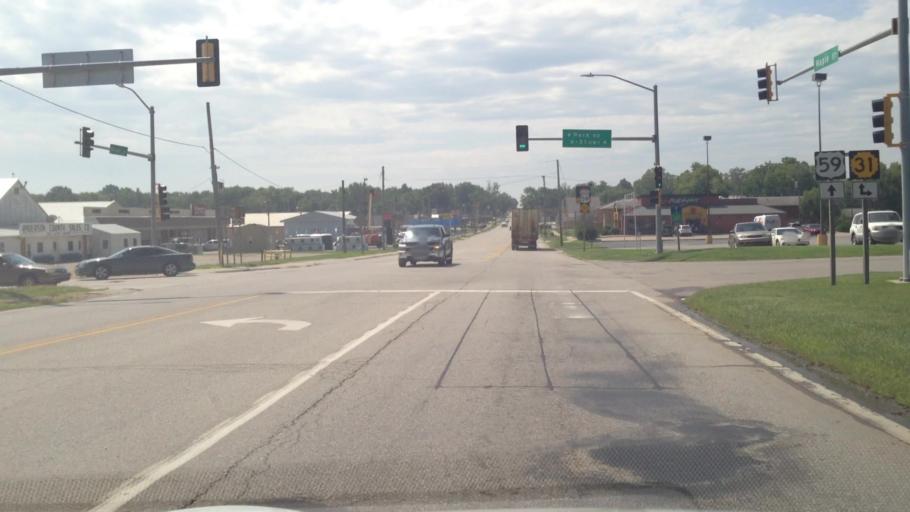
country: US
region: Kansas
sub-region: Anderson County
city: Garnett
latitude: 38.2886
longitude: -95.2493
